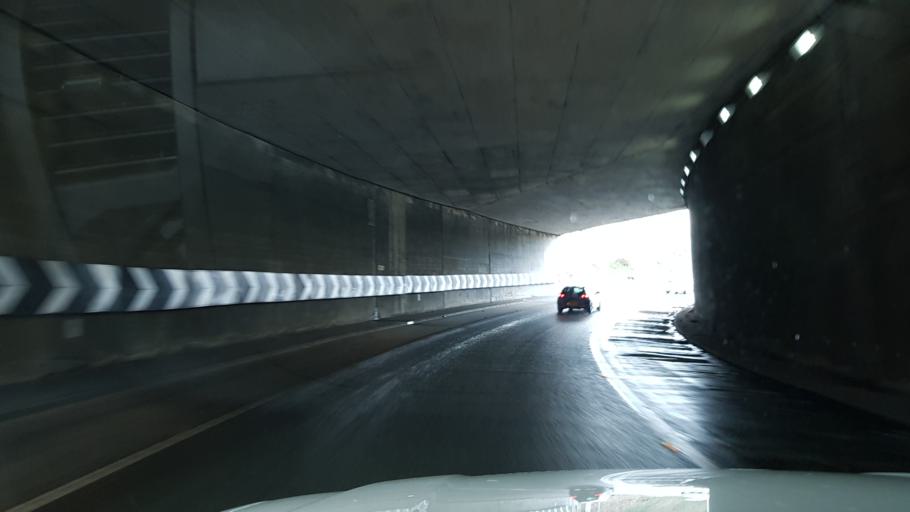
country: GB
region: England
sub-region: Liverpool
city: Liverpool
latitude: 53.4184
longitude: -2.9822
